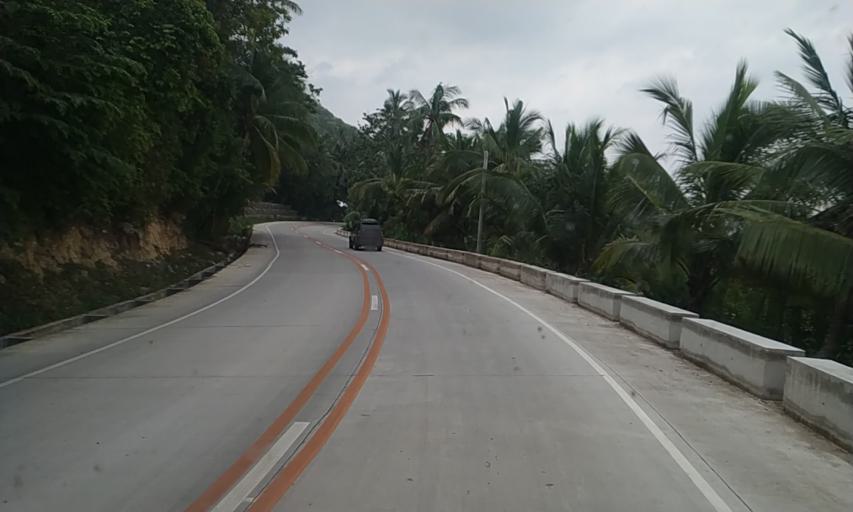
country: PH
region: Central Visayas
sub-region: Province of Negros Oriental
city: Basak
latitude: 10.2047
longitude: 123.3001
